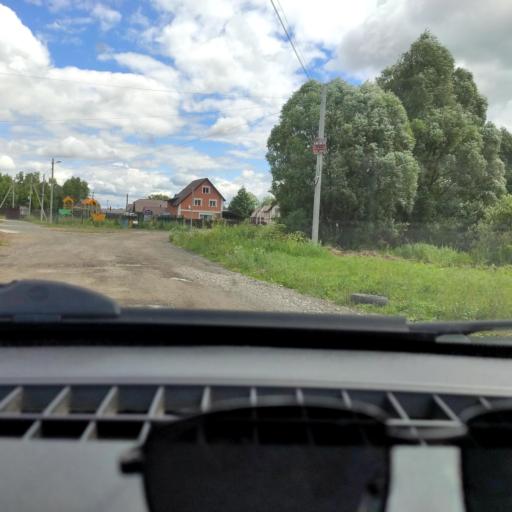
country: RU
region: Bashkortostan
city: Ufa
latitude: 54.6727
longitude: 56.0946
